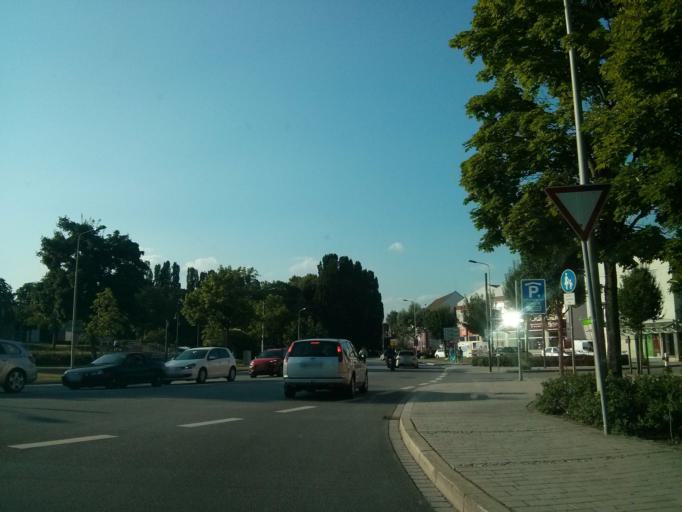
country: DE
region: Bavaria
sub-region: Lower Bavaria
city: Deggendorf
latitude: 48.8315
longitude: 12.9582
